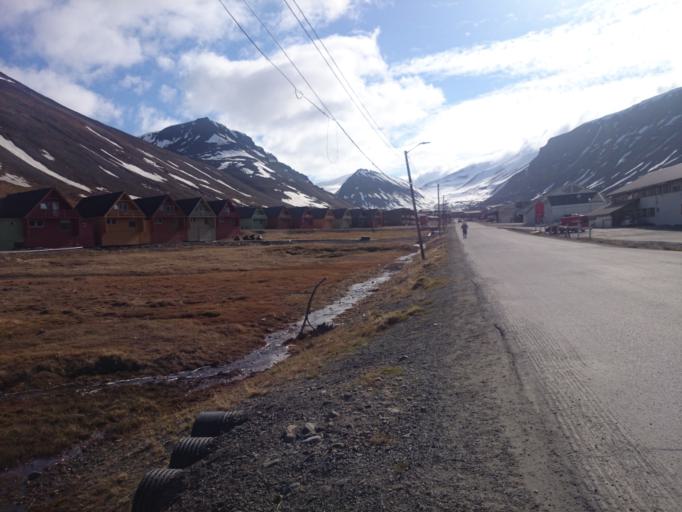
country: SJ
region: Svalbard
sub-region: Spitsbergen
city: Longyearbyen
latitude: 78.2192
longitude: 15.6460
